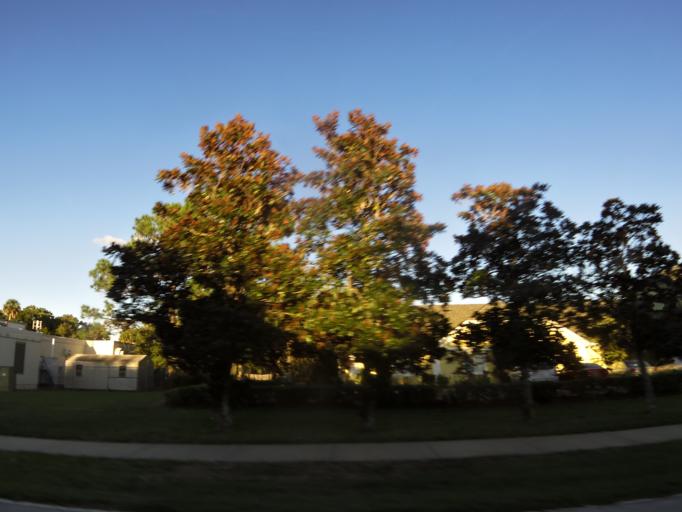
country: US
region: Florida
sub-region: Flagler County
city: Palm Coast
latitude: 29.5605
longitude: -81.2035
